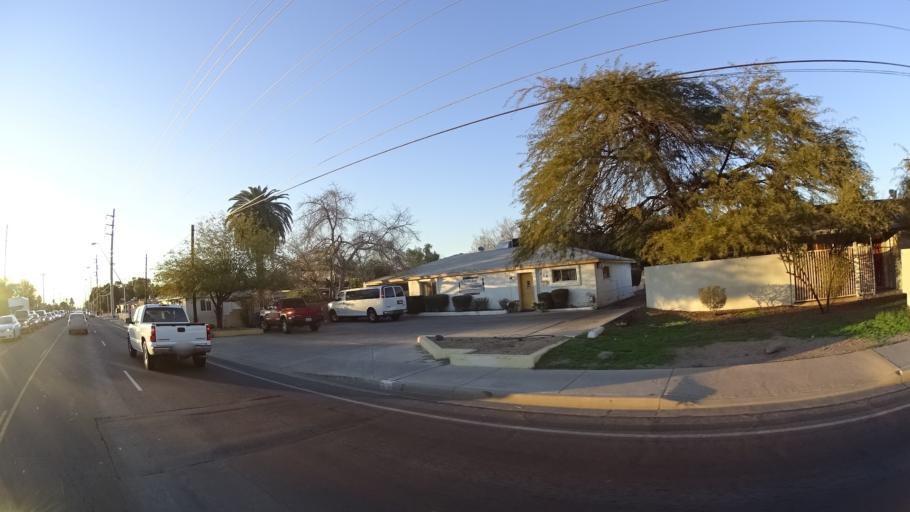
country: US
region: Arizona
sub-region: Maricopa County
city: Mesa
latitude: 33.4224
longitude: -111.8420
